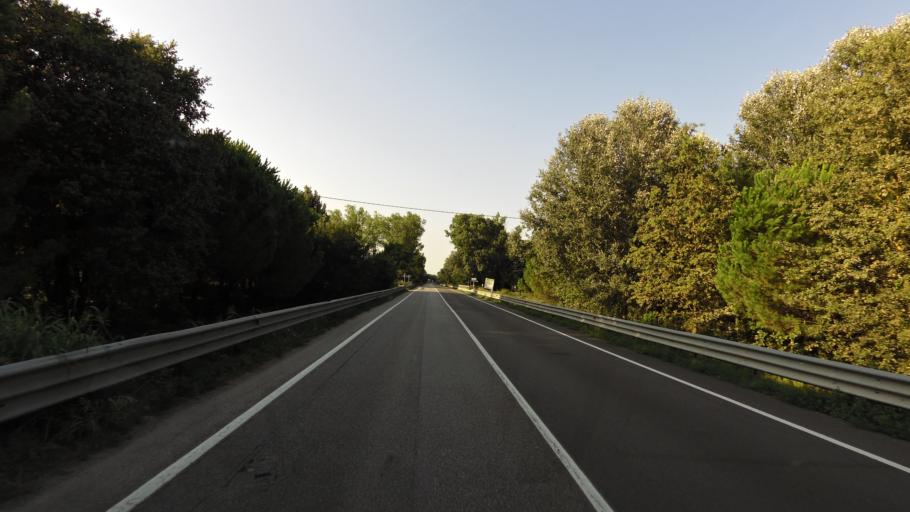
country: IT
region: Emilia-Romagna
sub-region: Provincia di Ravenna
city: Marina Romea
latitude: 44.4835
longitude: 12.2120
